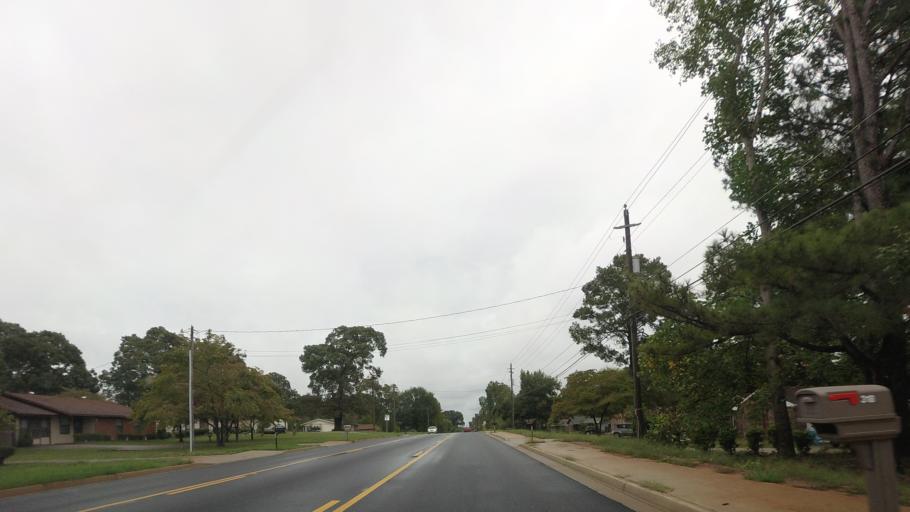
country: US
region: Georgia
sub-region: Houston County
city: Warner Robins
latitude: 32.5747
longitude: -83.6386
